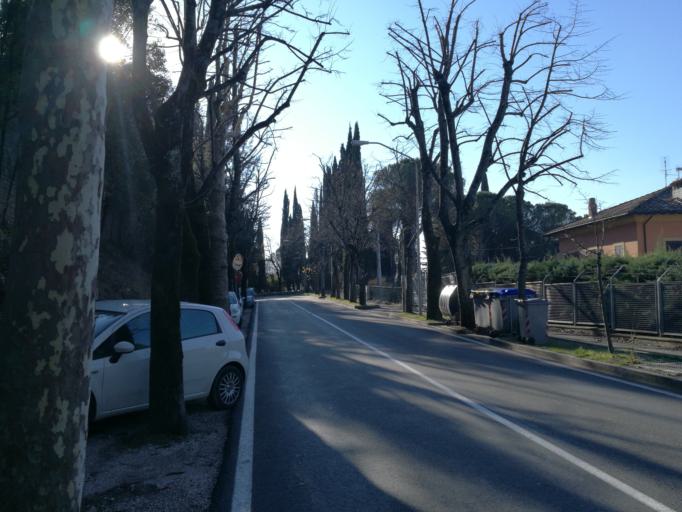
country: IT
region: Umbria
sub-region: Provincia di Perugia
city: Perugia
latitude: 43.1007
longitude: 12.3946
